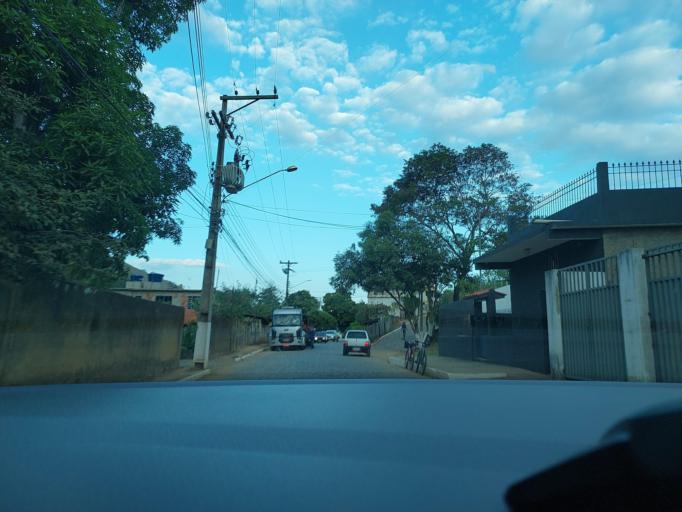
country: BR
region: Rio de Janeiro
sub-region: Natividade
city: Natividade
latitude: -21.1818
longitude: -42.1041
